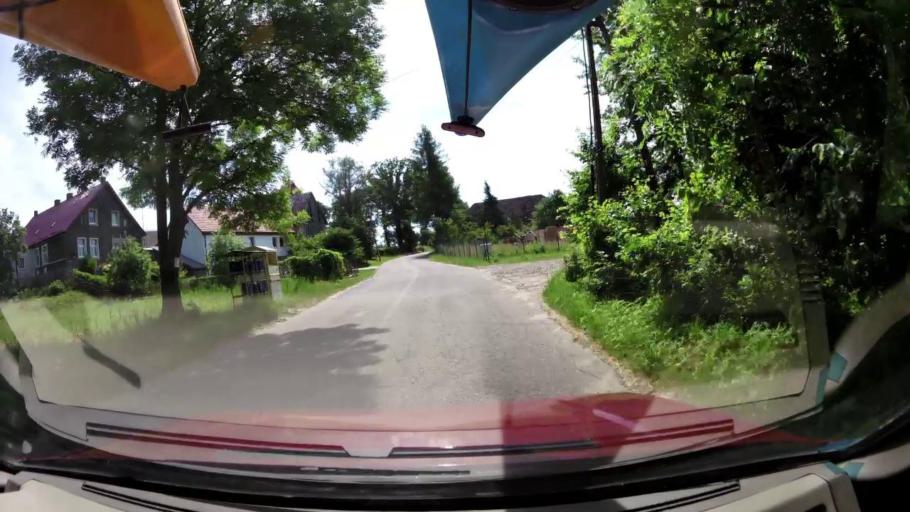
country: PL
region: West Pomeranian Voivodeship
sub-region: Powiat slawienski
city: Darlowo
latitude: 54.3175
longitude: 16.4170
